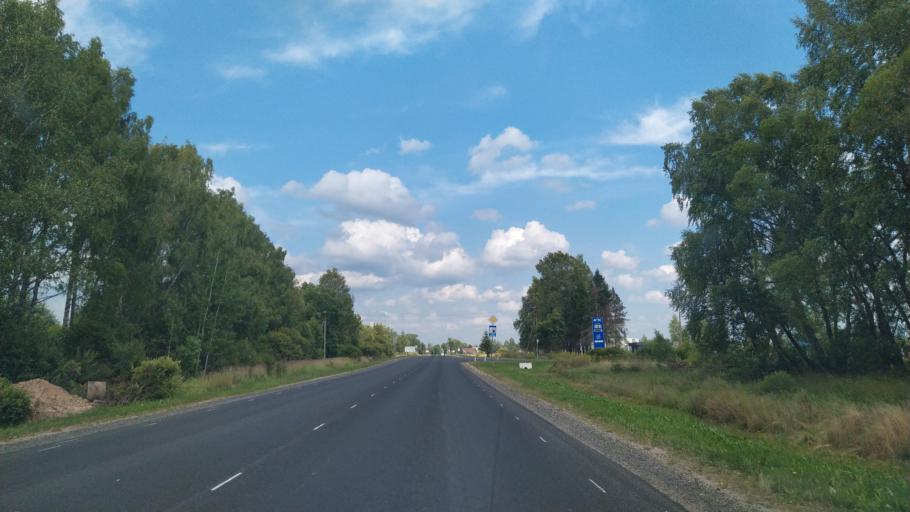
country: RU
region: Pskov
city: Porkhov
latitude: 57.7578
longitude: 29.5341
